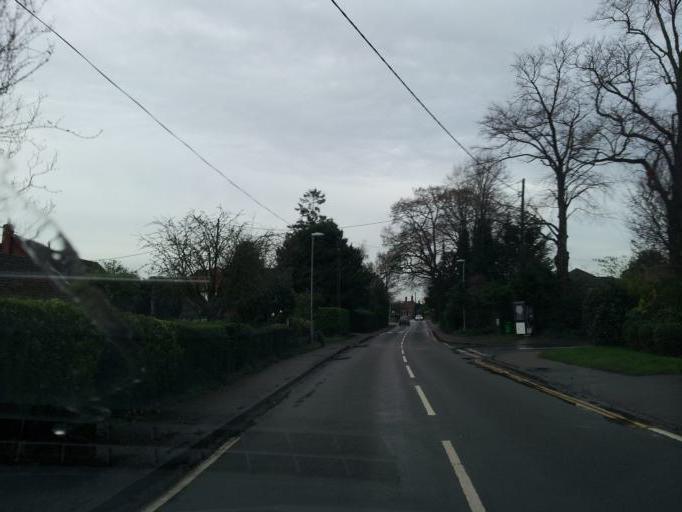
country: GB
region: England
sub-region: Norfolk
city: Brundall
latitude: 52.6225
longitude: 1.4391
